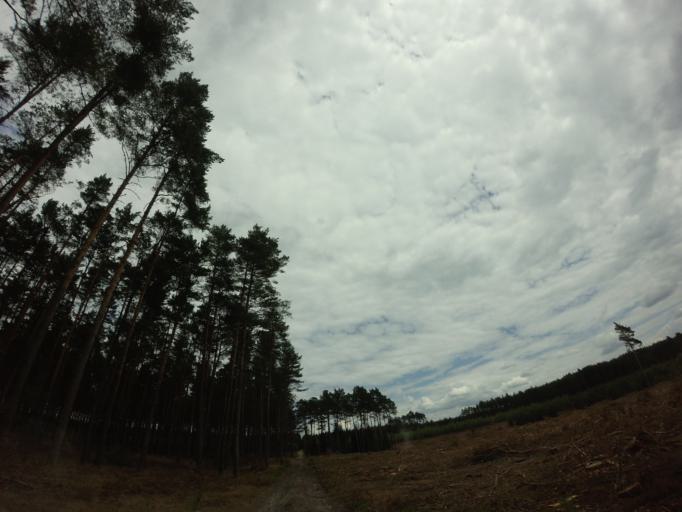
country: PL
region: West Pomeranian Voivodeship
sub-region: Powiat choszczenski
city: Drawno
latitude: 53.1487
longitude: 15.7764
